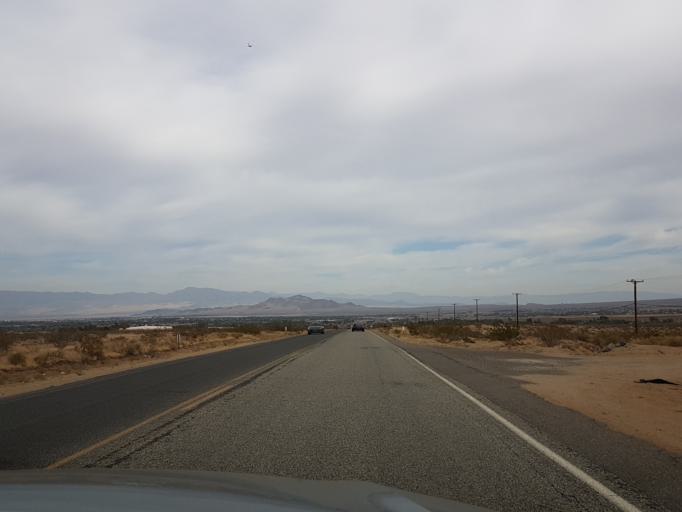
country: US
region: California
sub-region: Kern County
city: Ridgecrest
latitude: 35.5816
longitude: -117.7095
